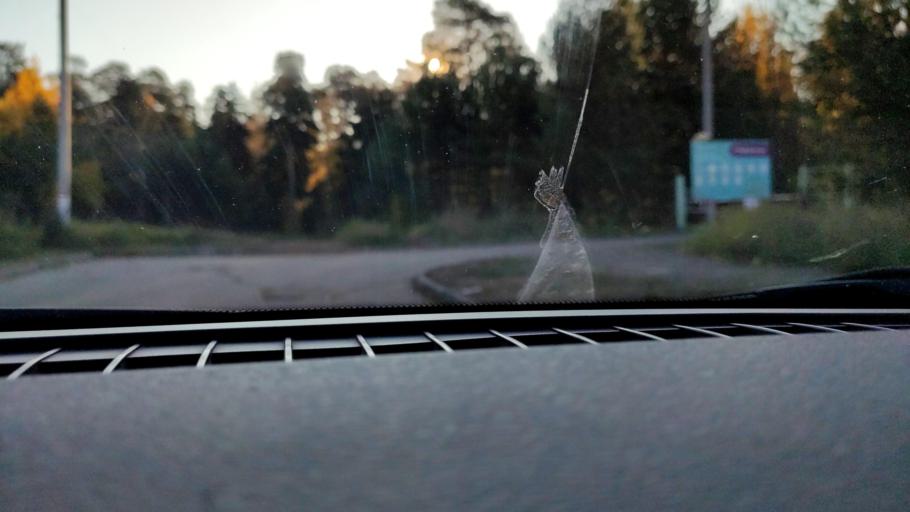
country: RU
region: Perm
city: Kondratovo
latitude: 57.9900
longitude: 56.1423
